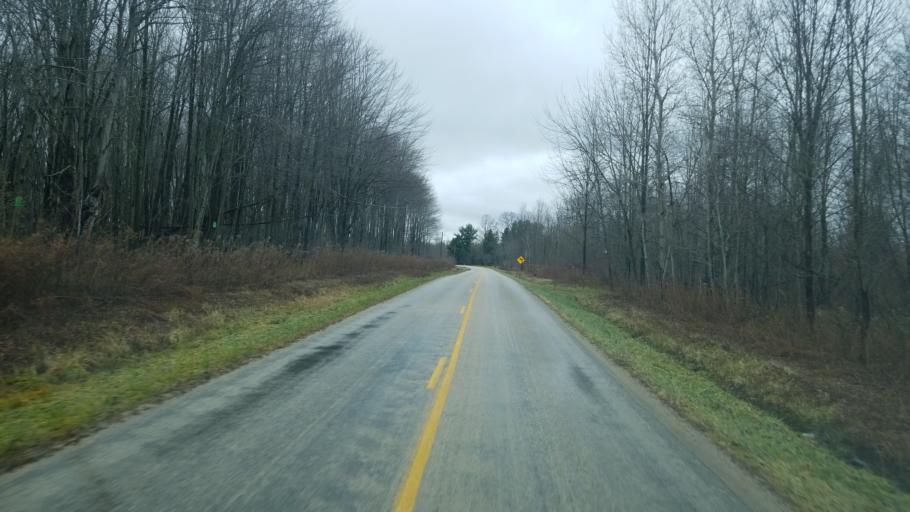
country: US
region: Ohio
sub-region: Ashtabula County
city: North Kingsville
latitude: 41.8127
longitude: -80.6246
